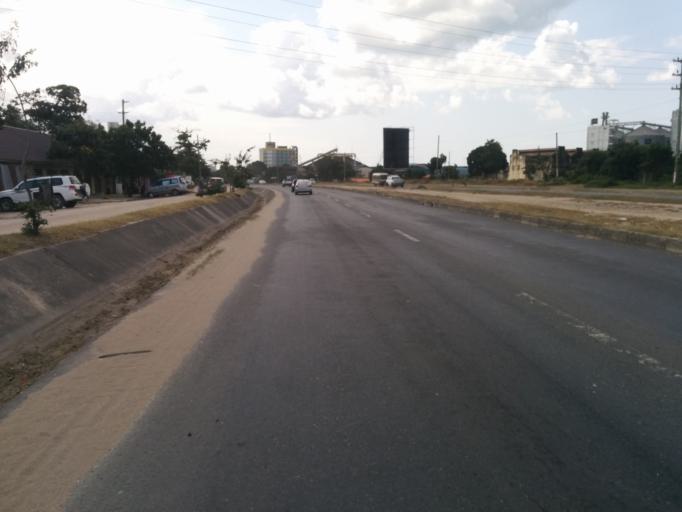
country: TZ
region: Dar es Salaam
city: Dar es Salaam
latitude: -6.8360
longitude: 39.2862
